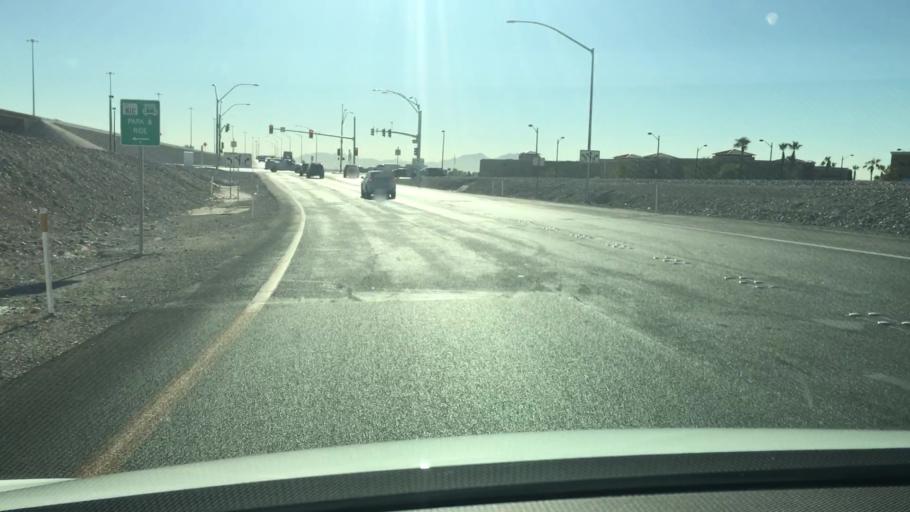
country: US
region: Nevada
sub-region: Clark County
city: Summerlin South
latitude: 36.2793
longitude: -115.2894
